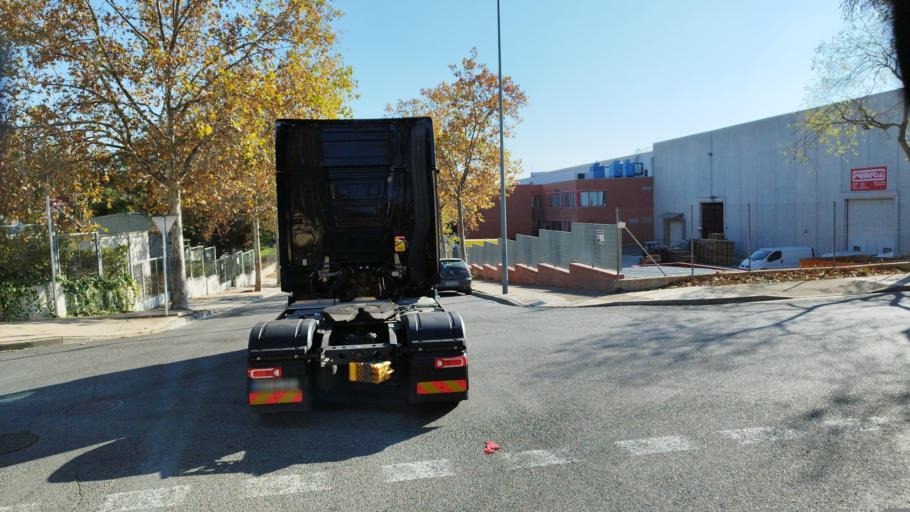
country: ES
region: Catalonia
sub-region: Provincia de Tarragona
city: Reus
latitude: 41.1604
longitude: 1.0761
